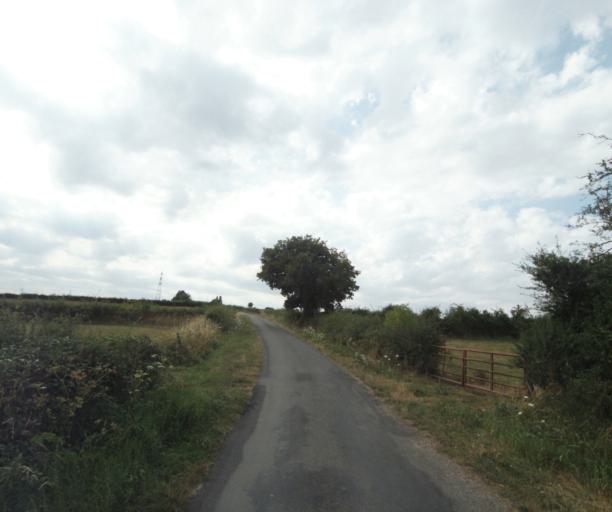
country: FR
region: Bourgogne
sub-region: Departement de Saone-et-Loire
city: Gueugnon
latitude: 46.5990
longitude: 4.0915
